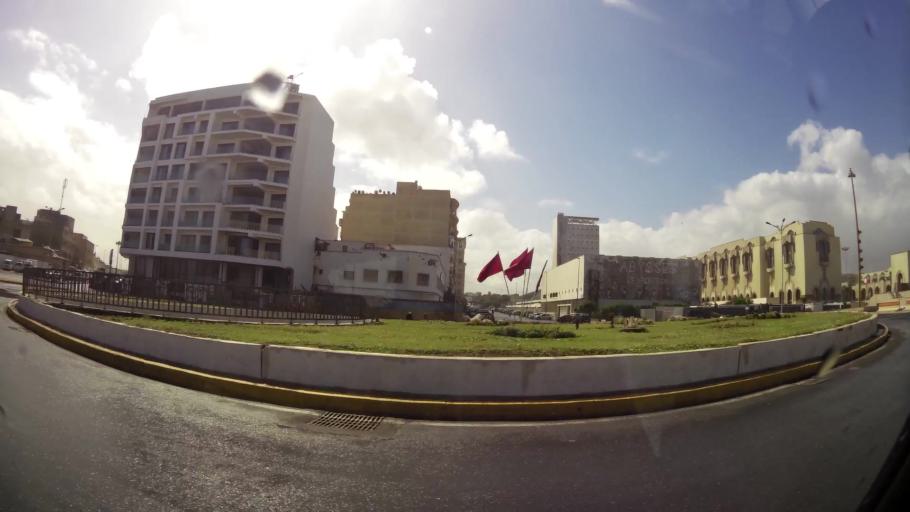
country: MA
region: Grand Casablanca
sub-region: Casablanca
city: Casablanca
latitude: 33.6078
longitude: -7.6305
